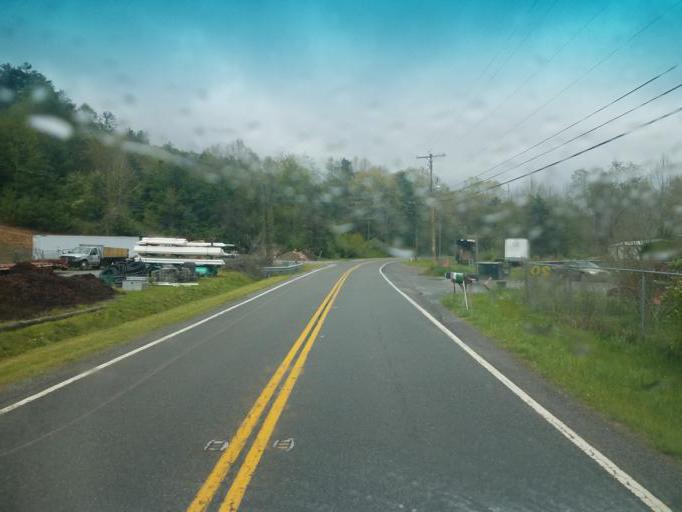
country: US
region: Virginia
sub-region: Bland County
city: Bland
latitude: 37.1595
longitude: -81.1497
